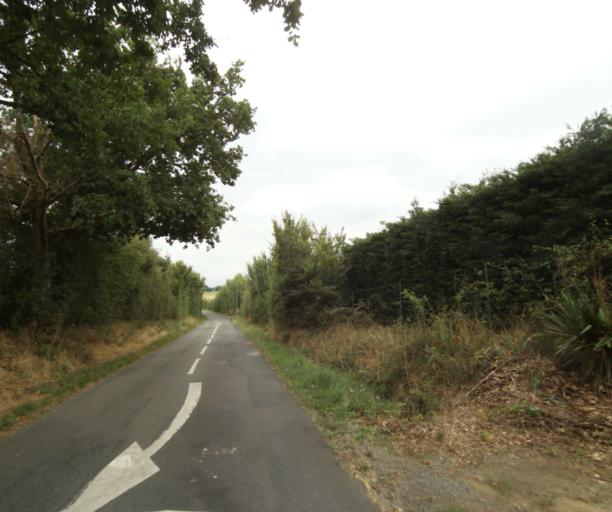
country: FR
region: Pays de la Loire
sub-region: Departement de la Sarthe
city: Solesmes
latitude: 47.8509
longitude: -0.2905
